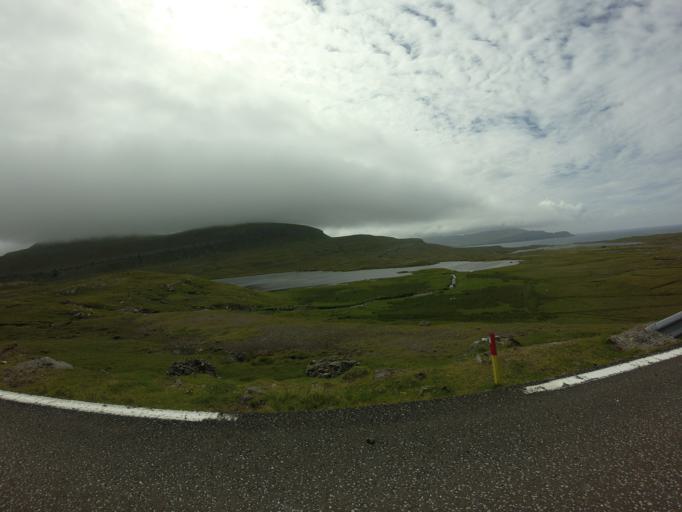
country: FO
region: Sandoy
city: Sandur
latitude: 61.8235
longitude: -6.7337
